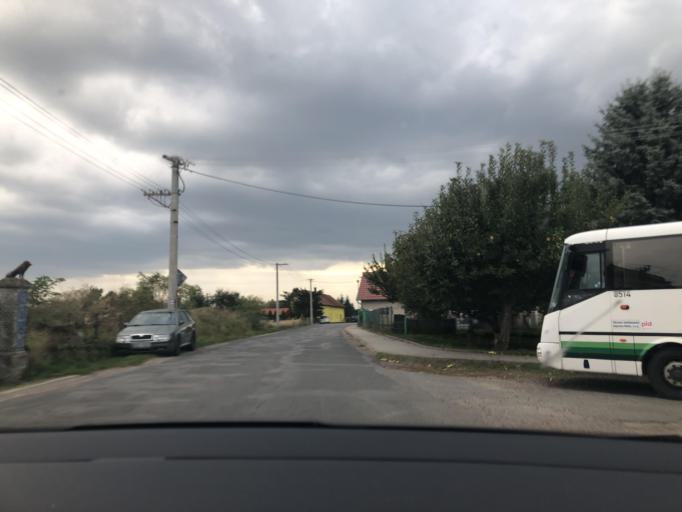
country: CZ
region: Pardubicky
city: Chvaletice
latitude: 50.0516
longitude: 15.4122
